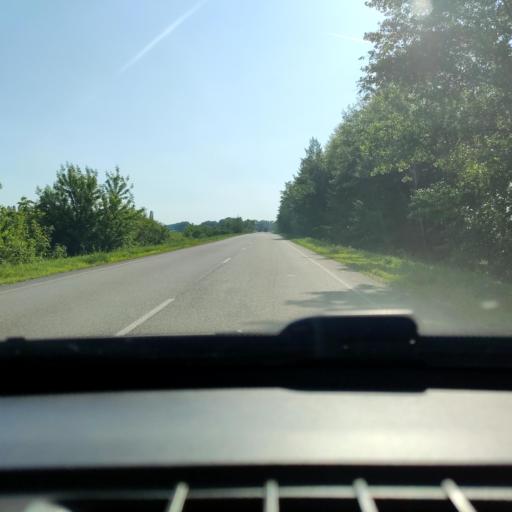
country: RU
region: Voronezj
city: Panino
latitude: 51.6285
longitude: 40.0493
